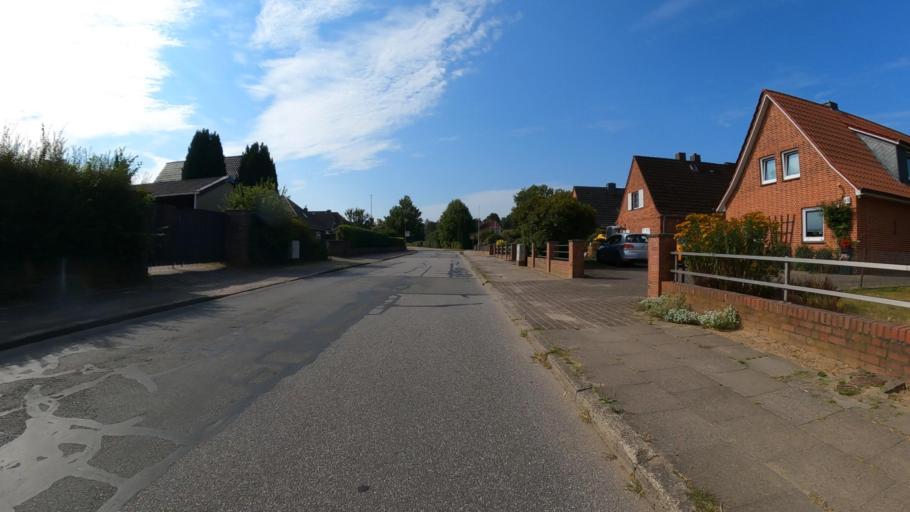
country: DE
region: Schleswig-Holstein
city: Hamwarde
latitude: 53.4488
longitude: 10.4196
